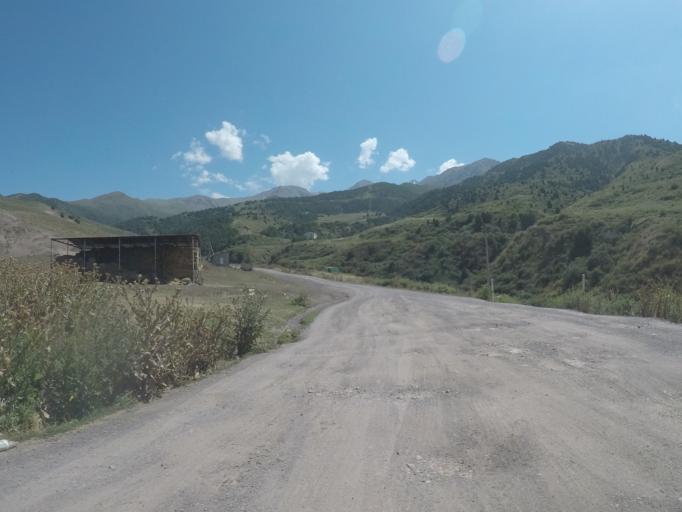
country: KG
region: Chuy
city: Bishkek
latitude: 42.6484
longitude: 74.5124
